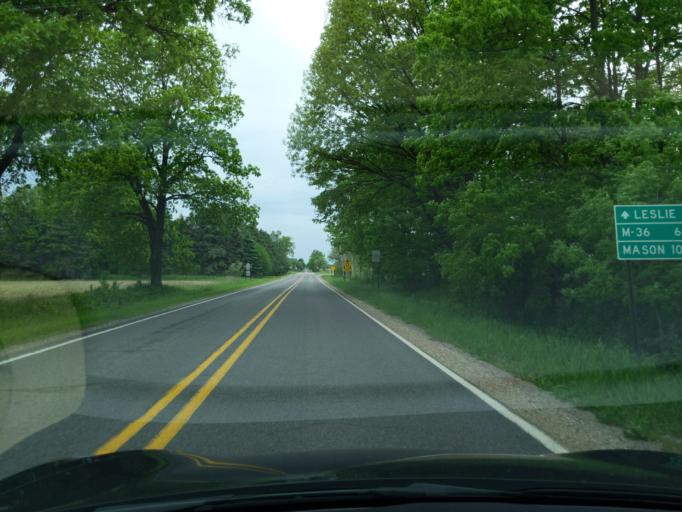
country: US
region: Michigan
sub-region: Ingham County
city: Leslie
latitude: 42.4679
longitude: -84.3536
